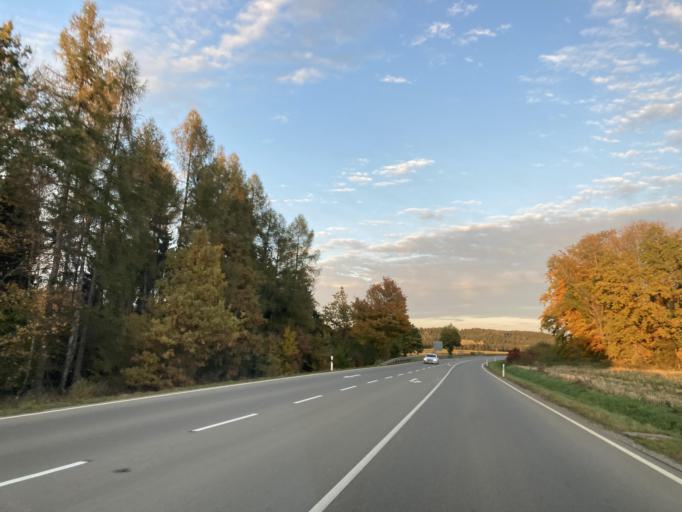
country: DE
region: Baden-Wuerttemberg
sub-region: Tuebingen Region
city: Zimmern unter der Burg
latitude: 48.2035
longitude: 8.7201
